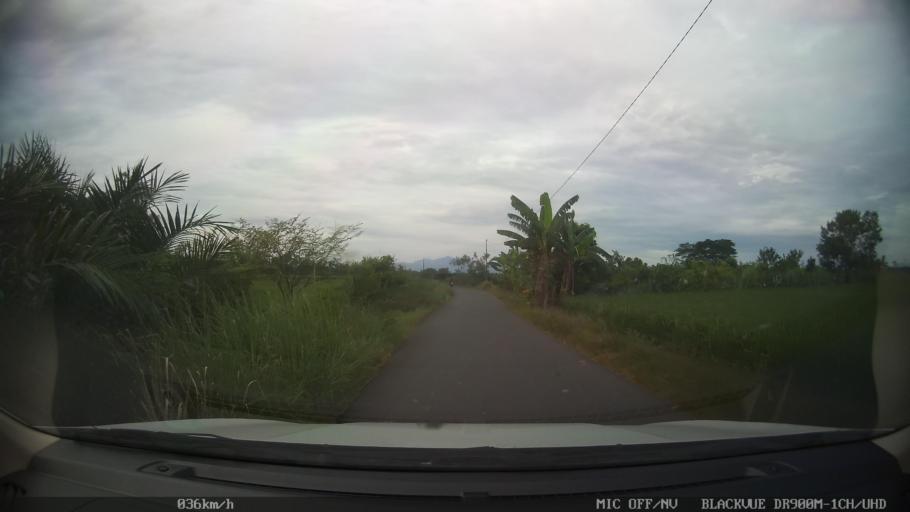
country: ID
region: North Sumatra
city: Sunggal
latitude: 3.5779
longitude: 98.5773
